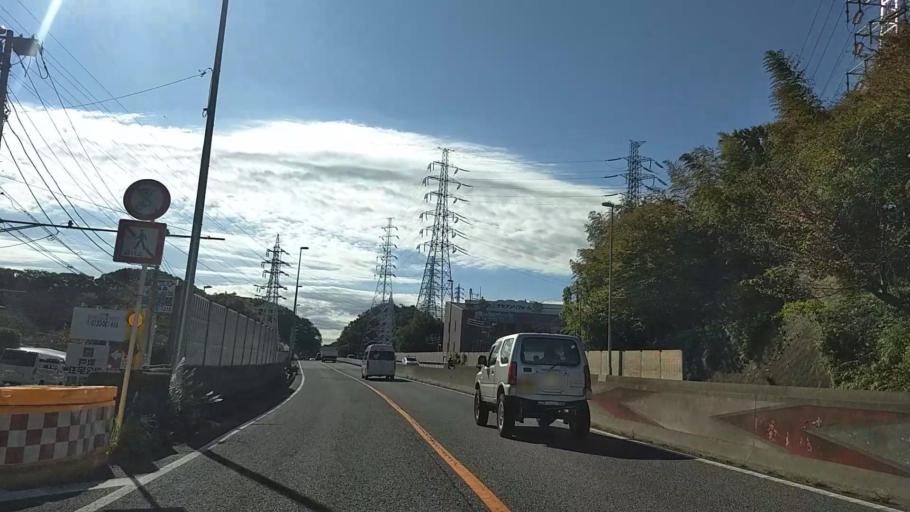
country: JP
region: Kanagawa
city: Fujisawa
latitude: 35.4017
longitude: 139.5274
